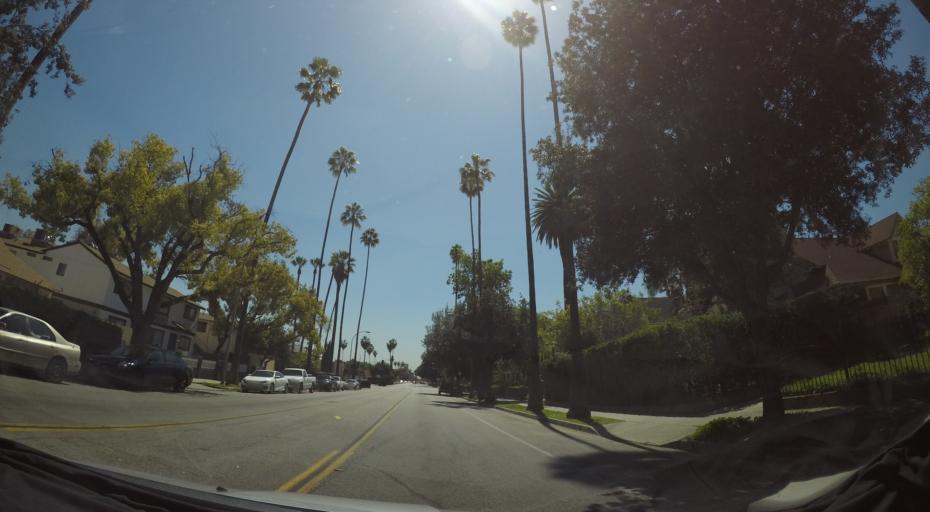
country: US
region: California
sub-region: Los Angeles County
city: Pasadena
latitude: 34.1554
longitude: -118.1415
